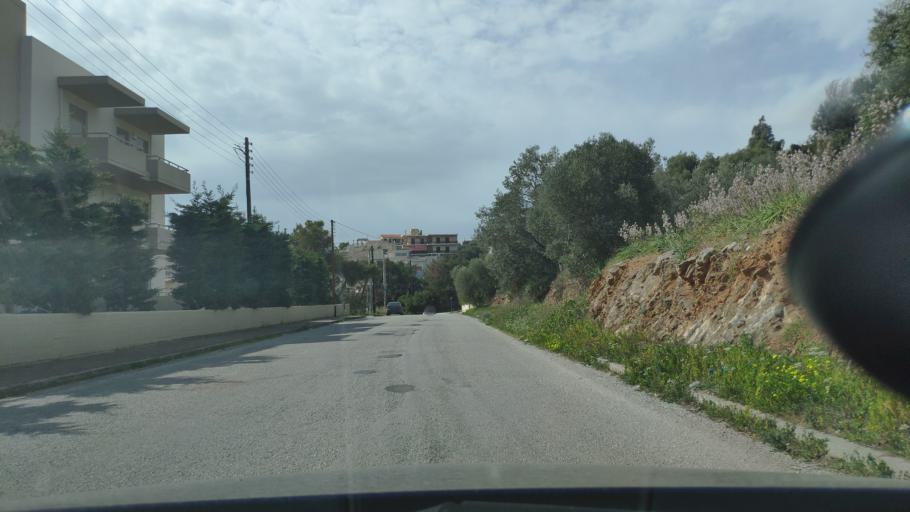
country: GR
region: Attica
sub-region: Nomarchia Anatolikis Attikis
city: Limin Mesoyaias
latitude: 37.8942
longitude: 24.0203
